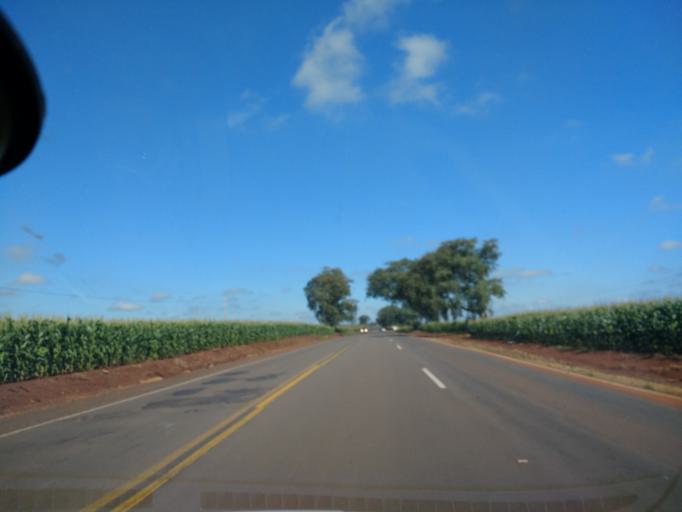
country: BR
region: Parana
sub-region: Terra Boa
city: Terra Boa
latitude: -23.6014
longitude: -52.4024
